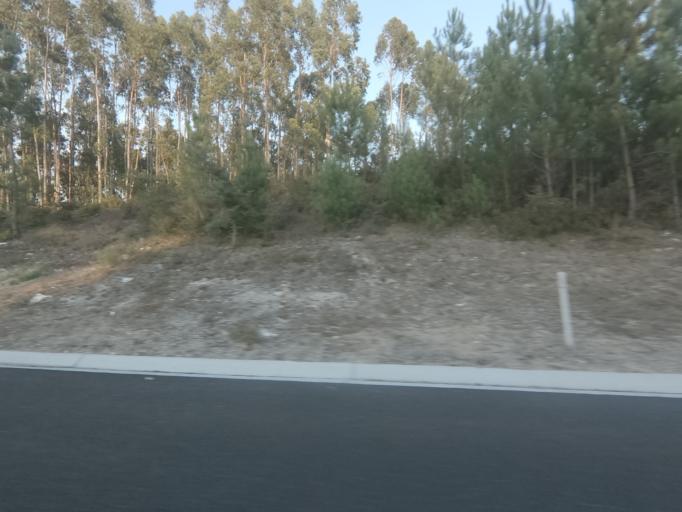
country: PT
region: Leiria
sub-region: Leiria
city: Caranguejeira
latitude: 39.7846
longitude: -8.7369
